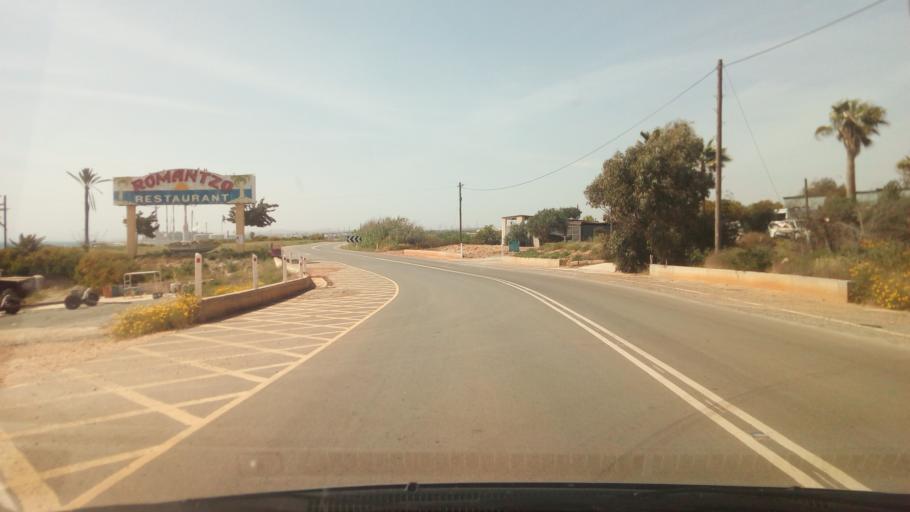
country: CY
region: Larnaka
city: Xylotymbou
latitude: 34.9808
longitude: 33.7700
